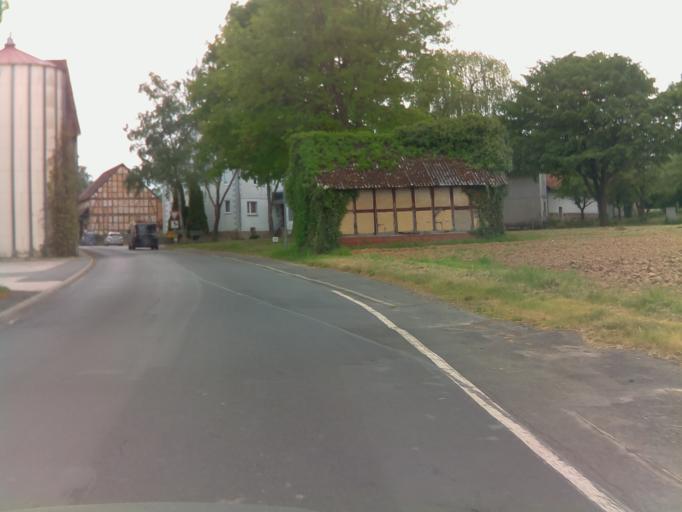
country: DE
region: Hesse
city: Schwalmstadt
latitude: 50.8876
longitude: 9.2314
